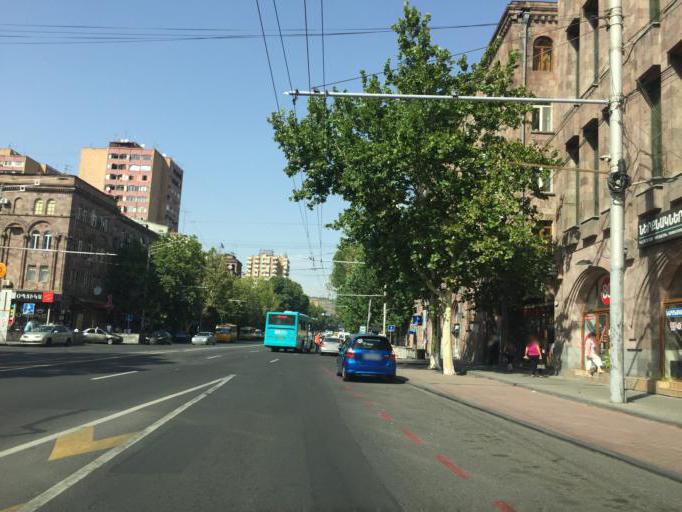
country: AM
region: Yerevan
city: Yerevan
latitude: 40.1779
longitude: 44.5043
